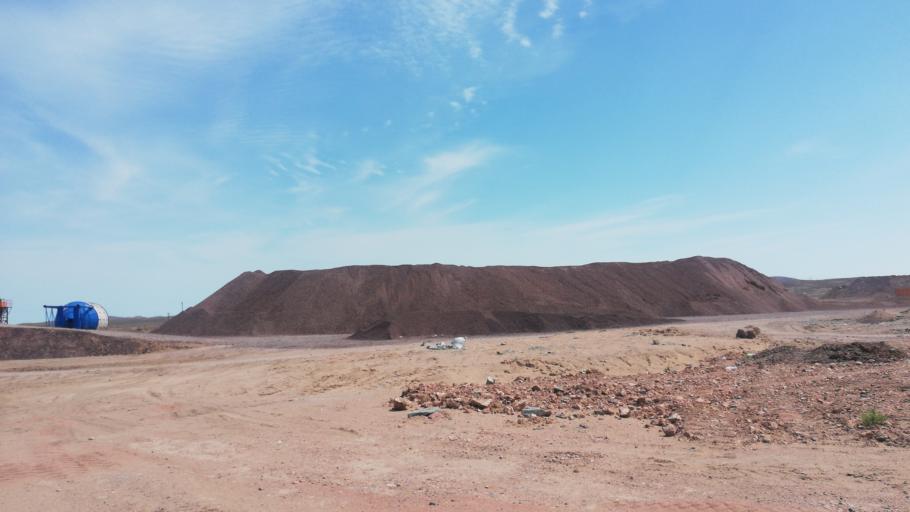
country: KZ
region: Qaraghandy
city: Balqash
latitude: 46.6433
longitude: 74.3944
